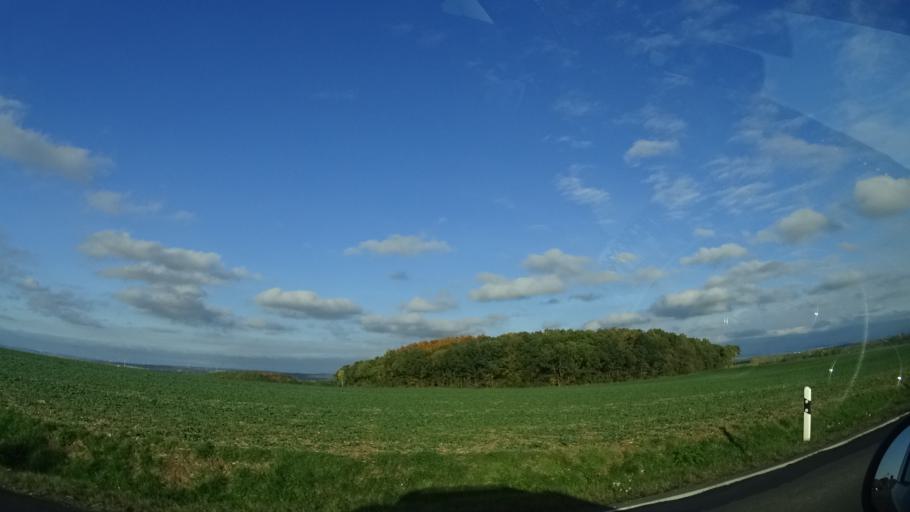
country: DE
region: Thuringia
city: Dornheim
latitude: 50.8302
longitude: 10.9712
